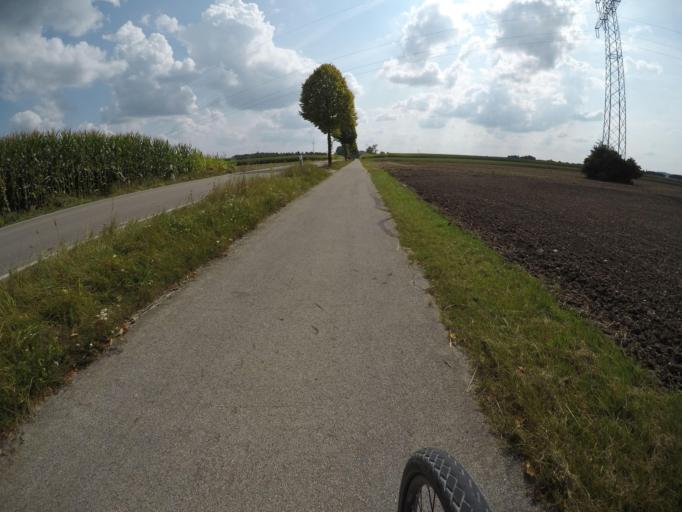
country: DE
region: Bavaria
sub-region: Swabia
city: Westendorf
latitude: 48.5580
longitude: 10.8442
